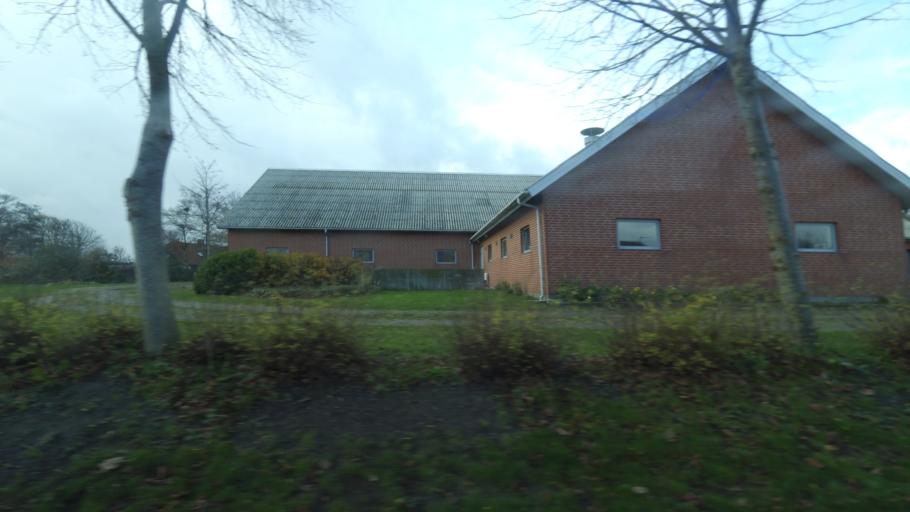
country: DK
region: Central Jutland
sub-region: Odder Kommune
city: Odder
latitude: 55.9537
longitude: 10.2402
